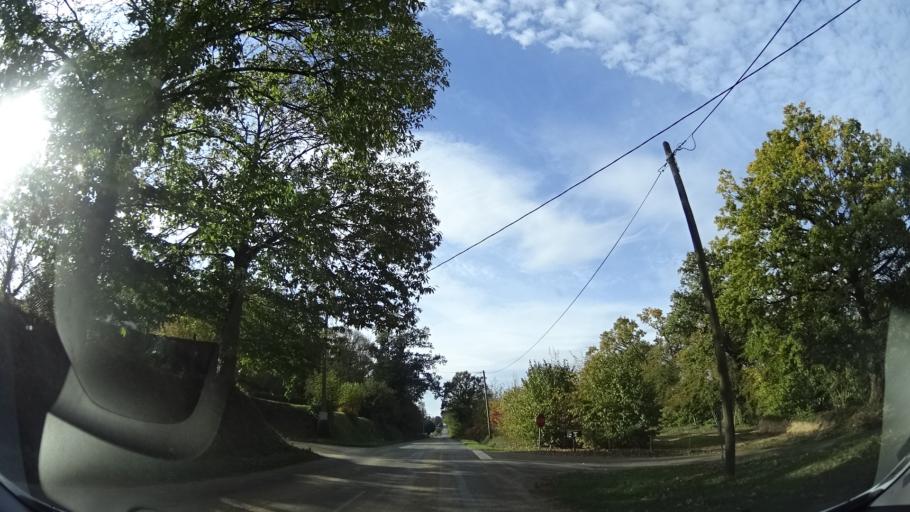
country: FR
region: Brittany
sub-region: Departement d'Ille-et-Vilaine
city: Geveze
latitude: 48.2161
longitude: -1.8328
